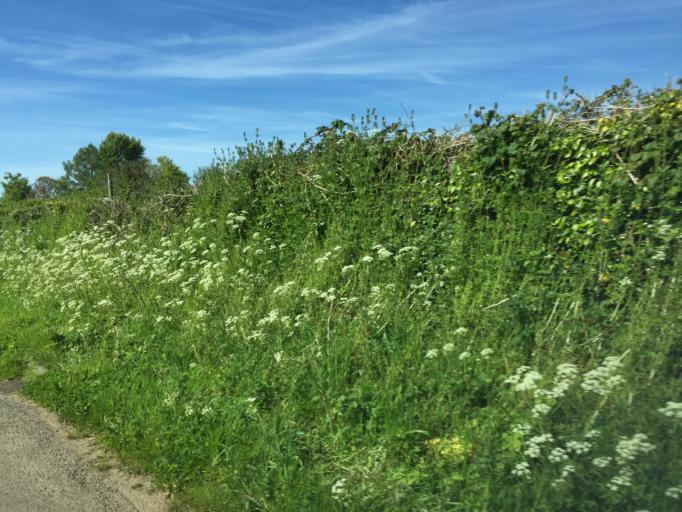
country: GB
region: England
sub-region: Wiltshire
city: Luckington
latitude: 51.5781
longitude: -2.2501
